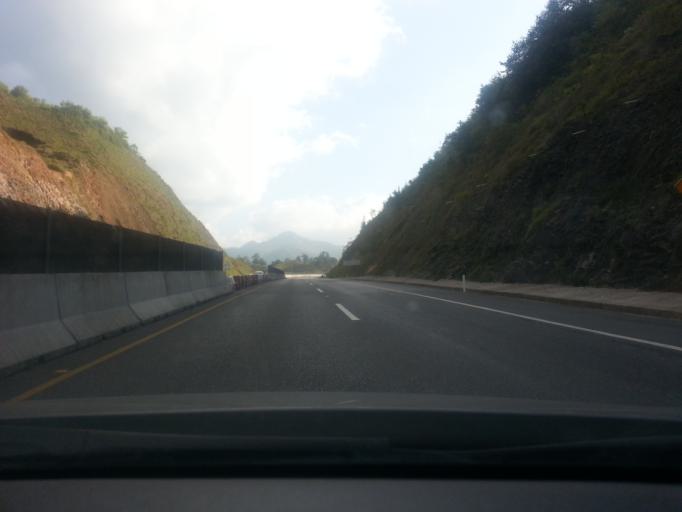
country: MX
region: Puebla
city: Xicotepec de Juarez
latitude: 20.2776
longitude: -97.9869
